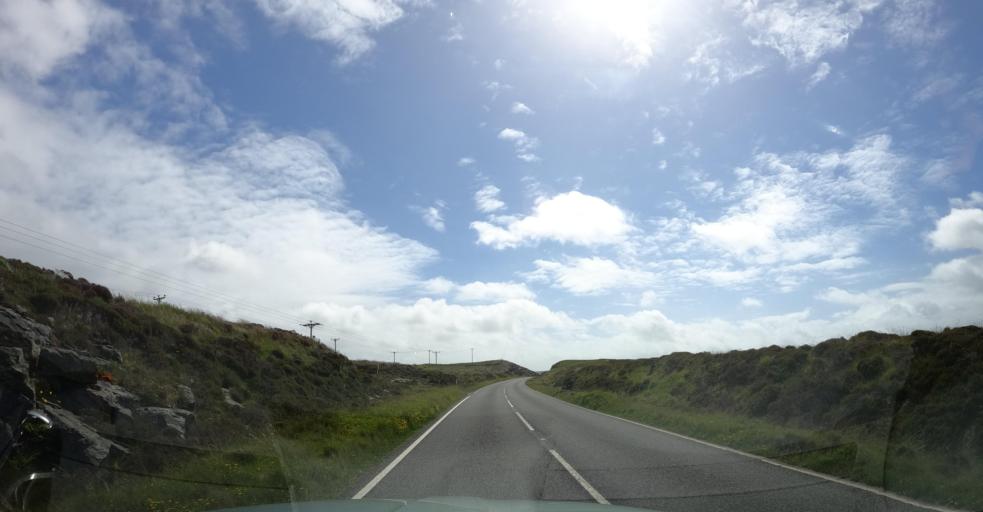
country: GB
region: Scotland
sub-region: Eilean Siar
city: Isle of South Uist
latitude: 57.2642
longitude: -7.3689
